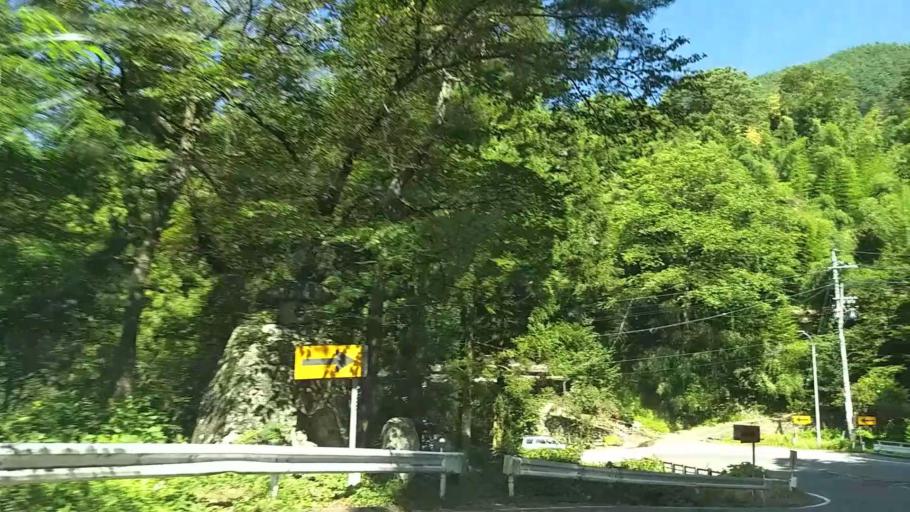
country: JP
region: Nagano
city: Matsumoto
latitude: 36.2205
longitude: 138.0418
